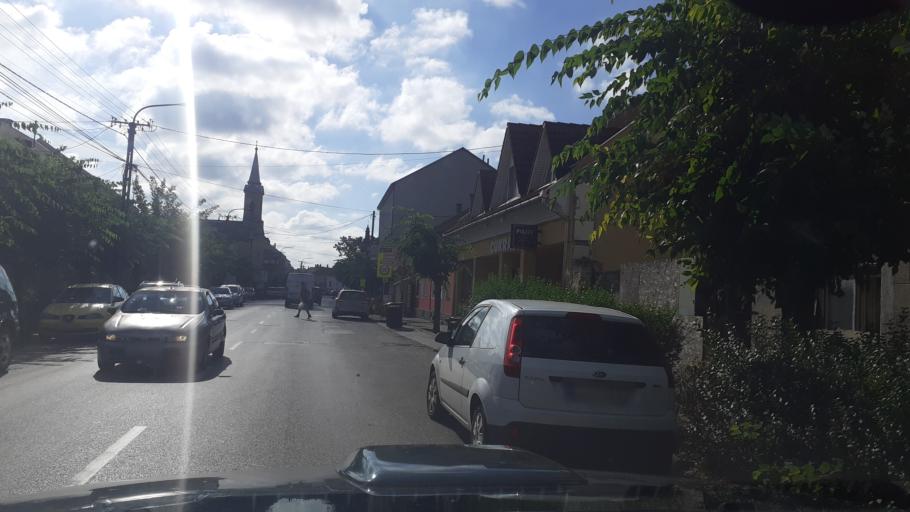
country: HU
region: Tolna
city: Dunafoldvar
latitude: 46.8095
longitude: 18.9225
